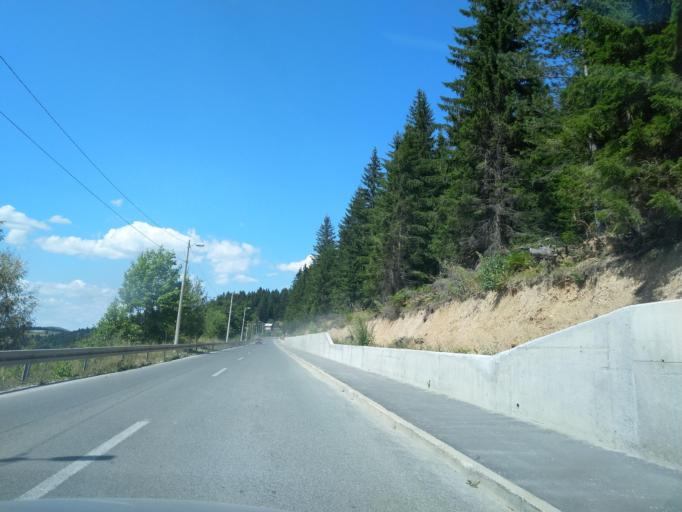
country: RS
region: Central Serbia
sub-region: Zlatiborski Okrug
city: Nova Varos
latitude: 43.4398
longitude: 19.8217
